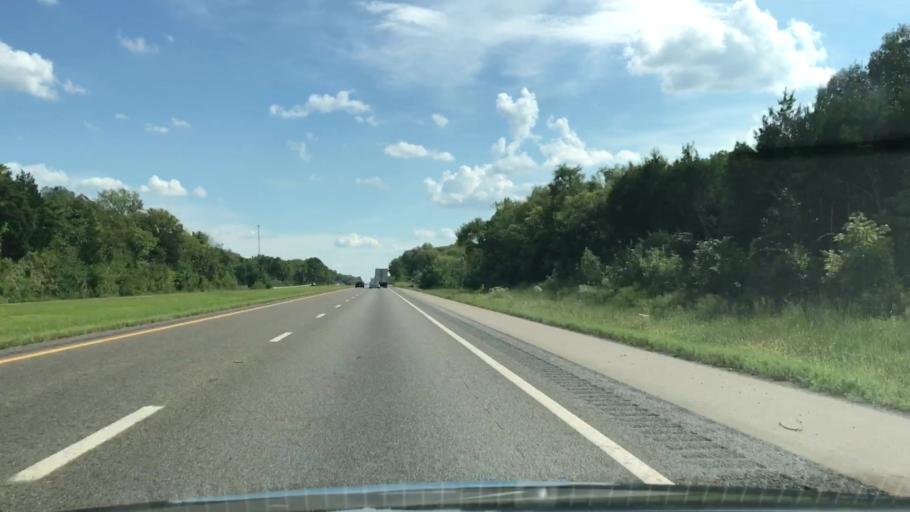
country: US
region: Tennessee
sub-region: Marshall County
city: Lewisburg
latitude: 35.4905
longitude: -86.8899
